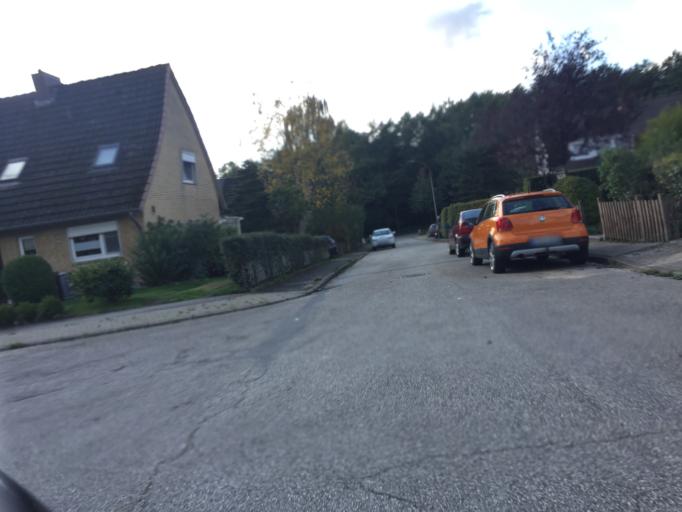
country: DE
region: Schleswig-Holstein
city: Heiligenstedten
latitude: 53.9398
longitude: 9.4931
